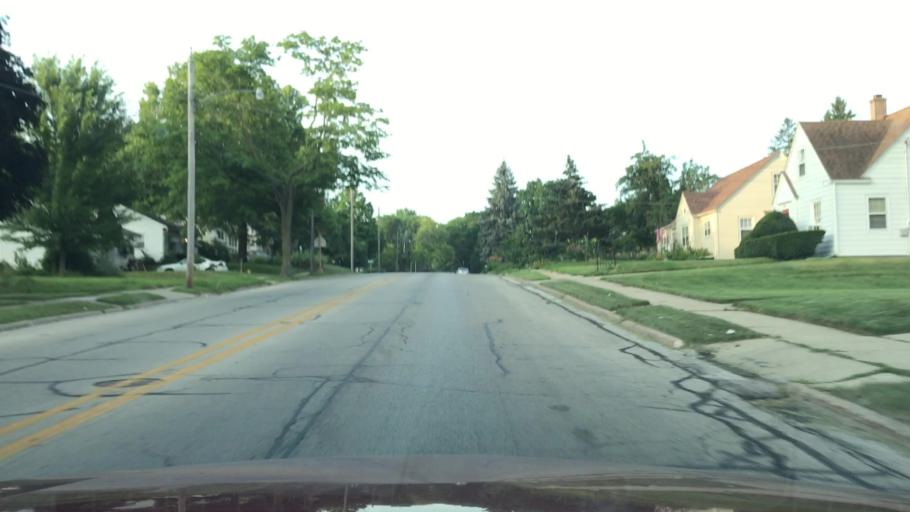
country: US
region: Illinois
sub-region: Winnebago County
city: Rockford
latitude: 42.2593
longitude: -89.0429
